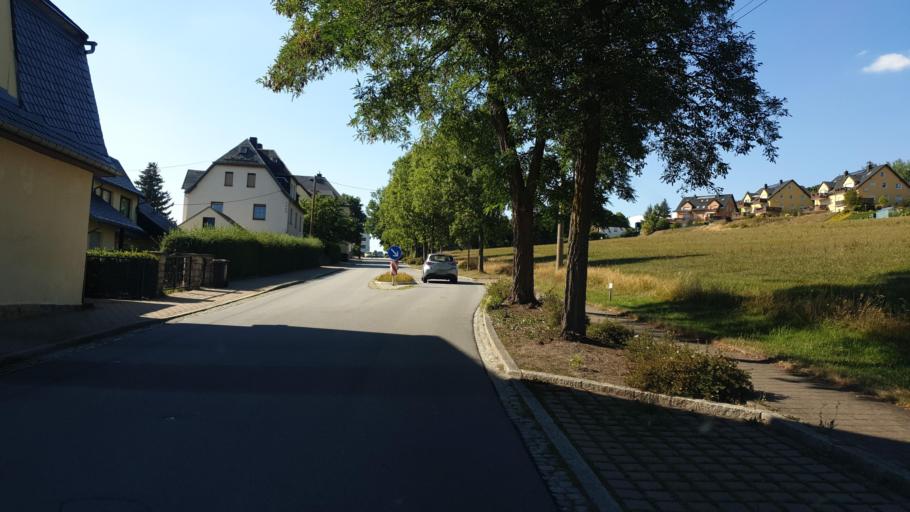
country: DE
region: Saxony
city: Bernsbach
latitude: 50.5783
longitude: 12.7696
